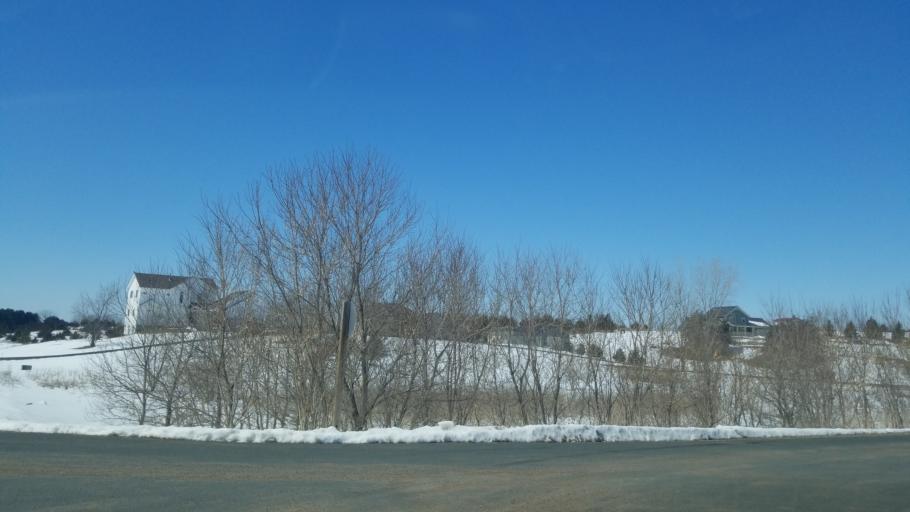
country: US
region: Wisconsin
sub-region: Saint Croix County
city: North Hudson
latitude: 44.9936
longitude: -92.6580
